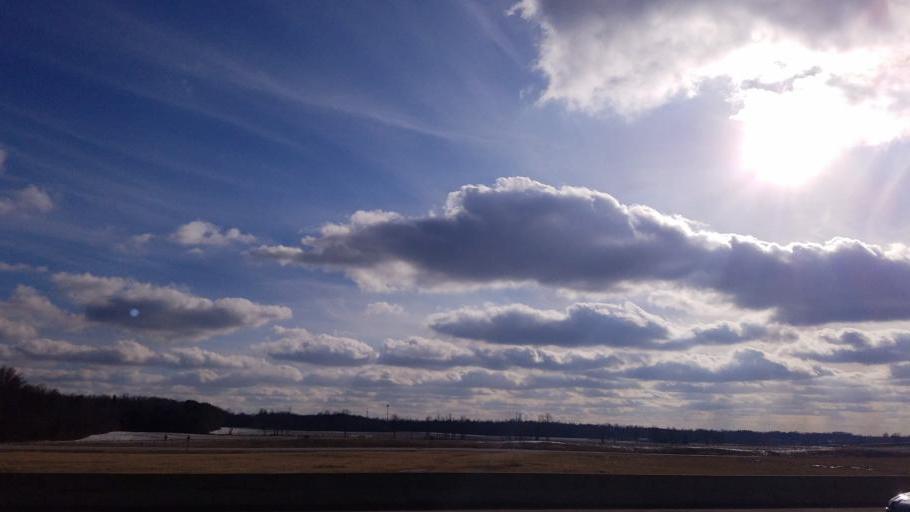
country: US
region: Ohio
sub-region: Richland County
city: Ontario
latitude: 40.7798
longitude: -82.6585
